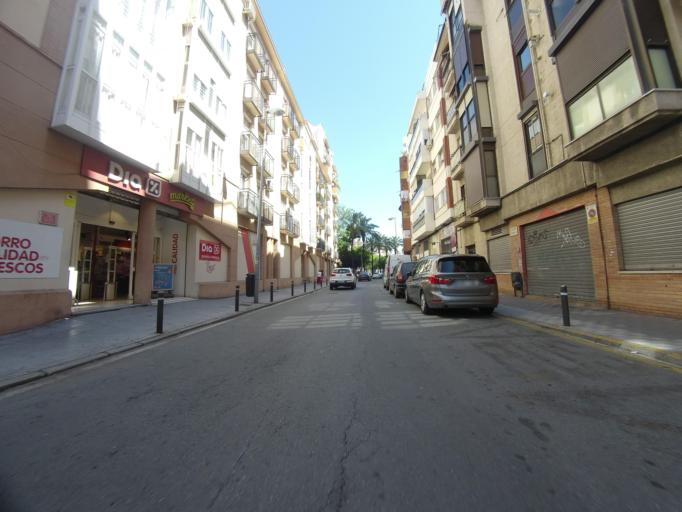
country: ES
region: Andalusia
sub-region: Provincia de Huelva
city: Huelva
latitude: 37.2624
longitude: -6.9538
